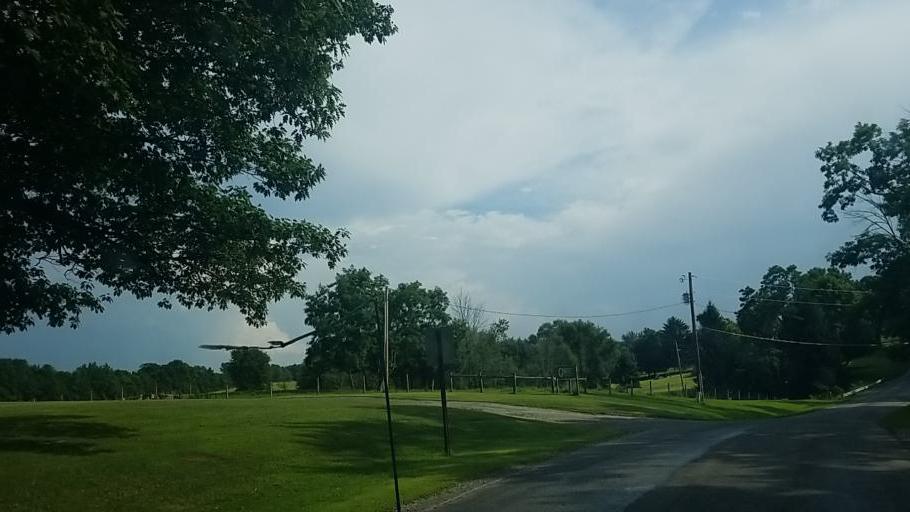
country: US
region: Ohio
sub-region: Wayne County
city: Creston
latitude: 40.9362
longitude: -81.9363
